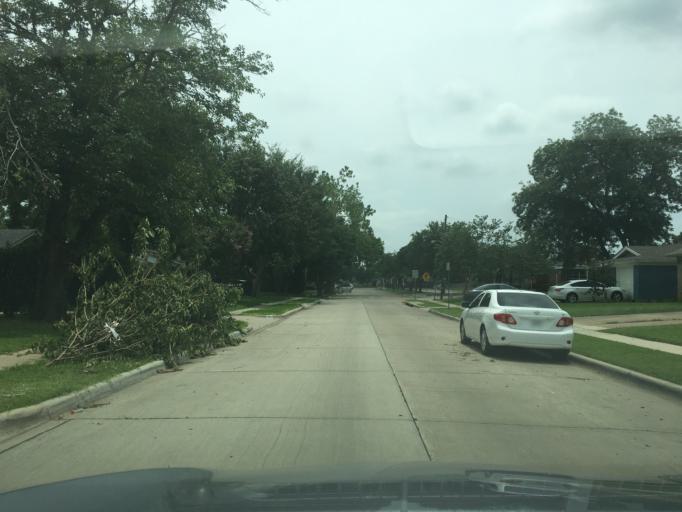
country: US
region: Texas
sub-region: Dallas County
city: Richardson
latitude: 32.9457
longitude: -96.7585
